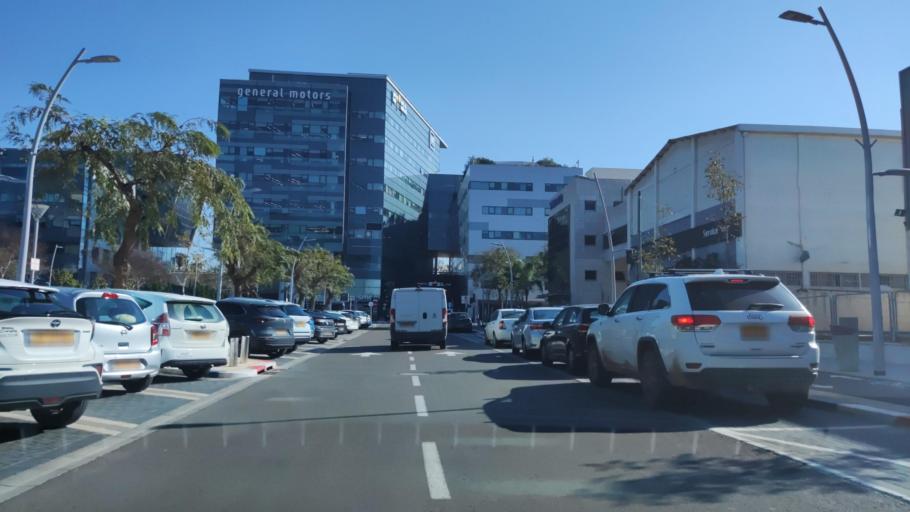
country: IL
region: Tel Aviv
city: Herzliya Pituah
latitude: 32.1584
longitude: 34.8072
